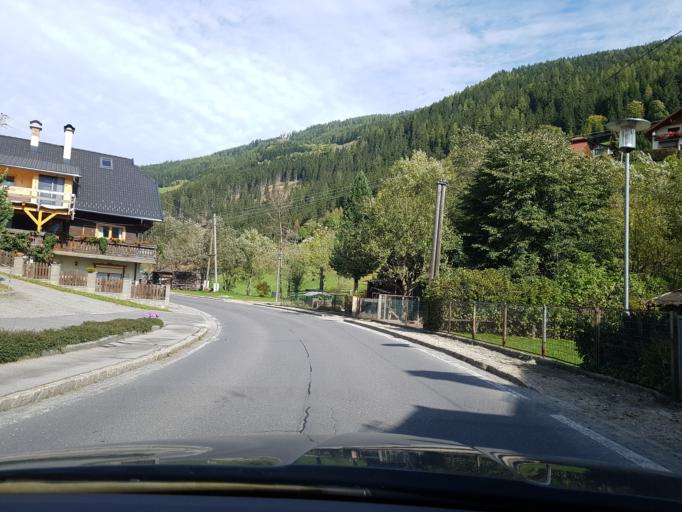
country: AT
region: Carinthia
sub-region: Politischer Bezirk Spittal an der Drau
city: Kleinkirchheim
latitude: 46.8572
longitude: 13.8921
